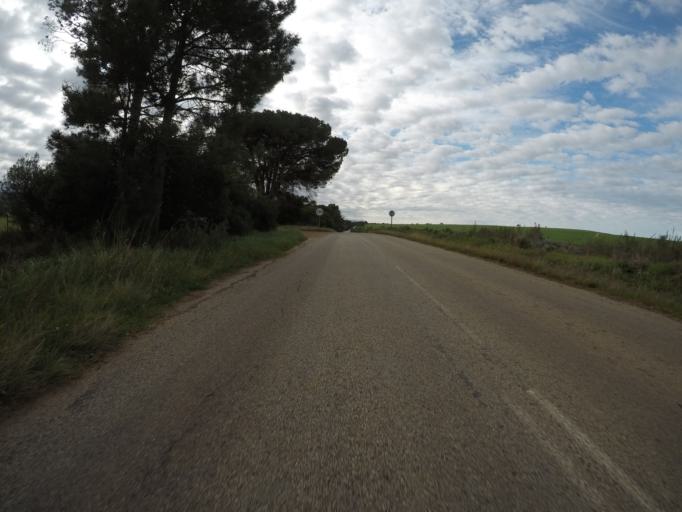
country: ZA
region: Eastern Cape
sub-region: Cacadu District Municipality
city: Kareedouw
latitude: -34.0057
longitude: 24.2418
